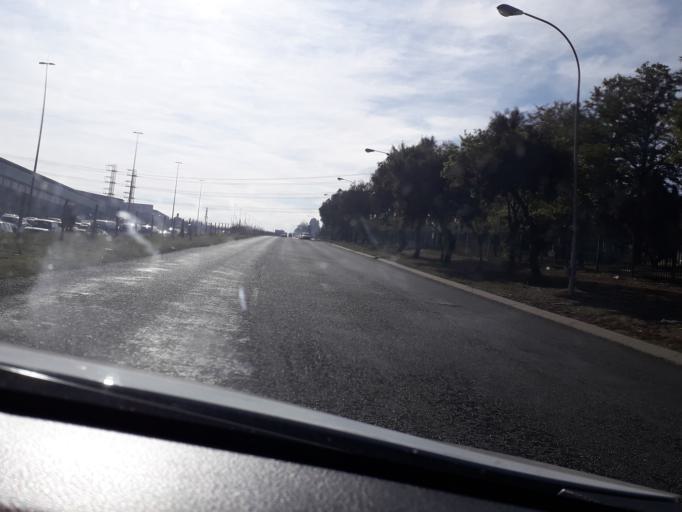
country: ZA
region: Gauteng
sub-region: Ekurhuleni Metropolitan Municipality
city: Germiston
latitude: -26.1644
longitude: 28.1750
